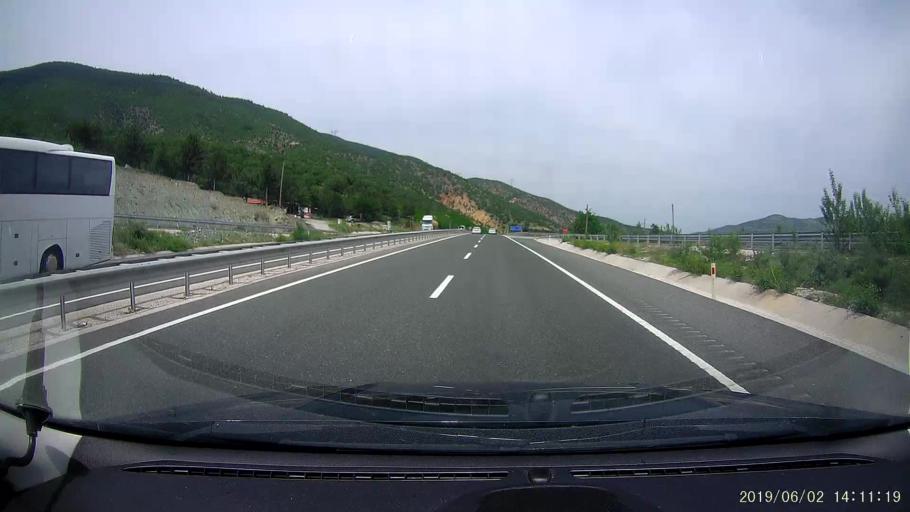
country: TR
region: Cankiri
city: Yaprakli
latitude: 40.9077
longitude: 33.7816
